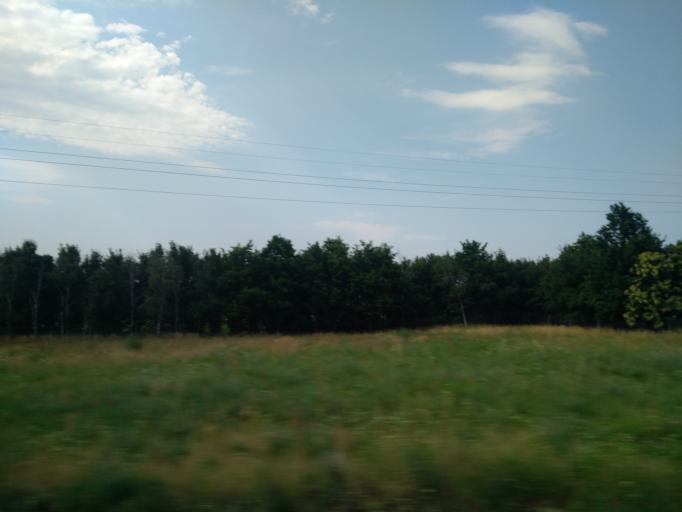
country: FR
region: Rhone-Alpes
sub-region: Departement du Rhone
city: Communay
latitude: 45.5888
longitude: 4.8289
